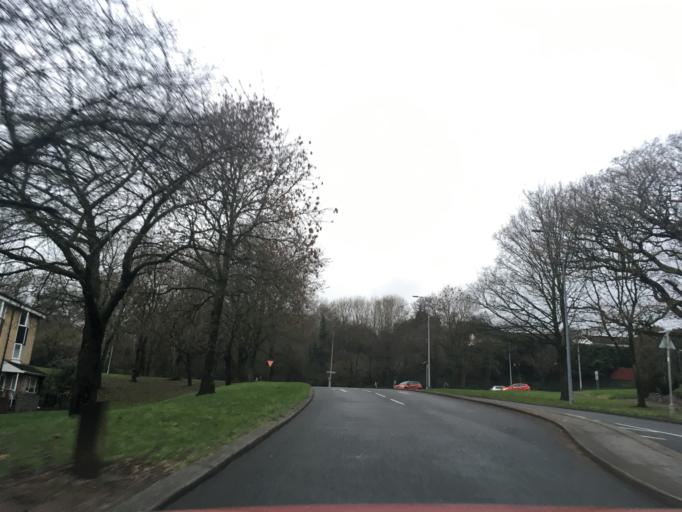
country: GB
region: Wales
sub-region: Cardiff
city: Cardiff
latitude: 51.5206
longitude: -3.1521
